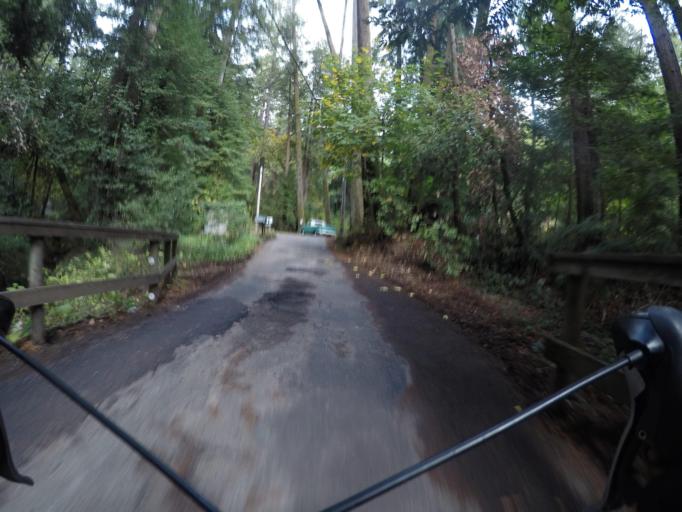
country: US
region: California
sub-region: Santa Cruz County
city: Ben Lomond
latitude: 37.0989
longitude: -122.0865
